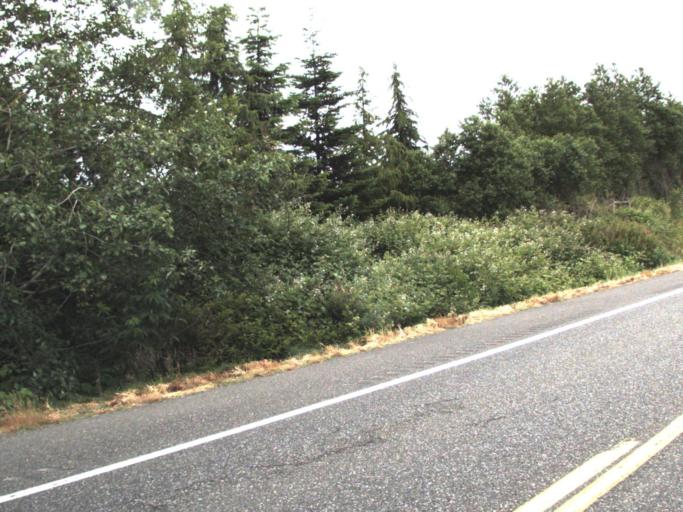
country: US
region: Washington
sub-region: Whatcom County
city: Birch Bay
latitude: 48.8921
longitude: -122.6845
